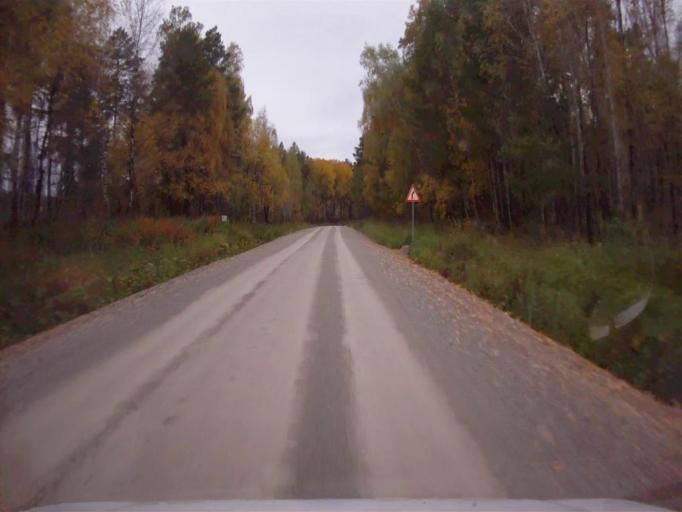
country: RU
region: Chelyabinsk
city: Nyazepetrovsk
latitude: 56.0670
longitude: 59.4370
